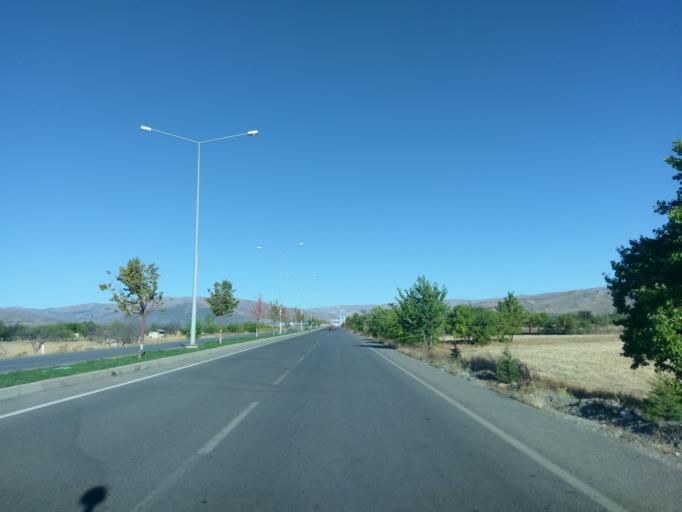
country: TR
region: Erzincan
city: Catalarmut
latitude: 39.7831
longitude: 39.4053
